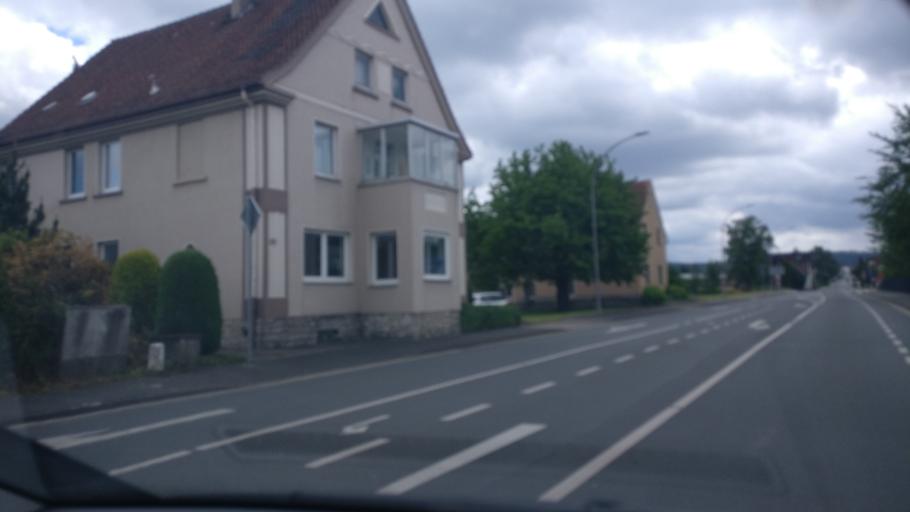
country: DE
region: North Rhine-Westphalia
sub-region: Regierungsbezirk Detmold
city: Leopoldshohe
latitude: 51.9821
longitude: 8.7146
